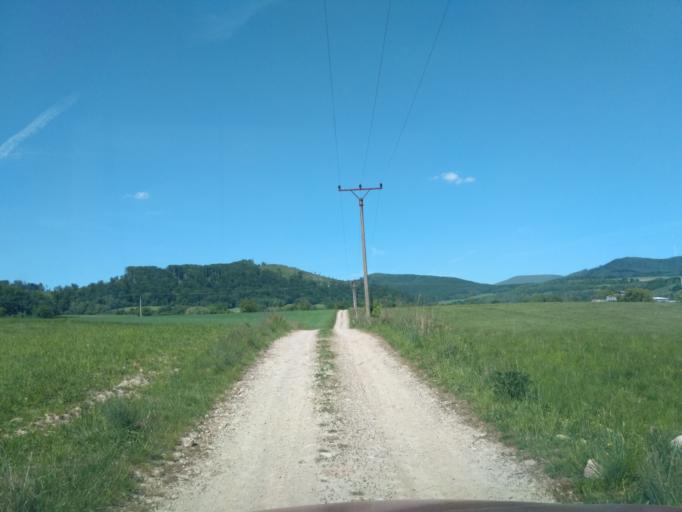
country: SK
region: Presovsky
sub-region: Okres Presov
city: Presov
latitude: 48.8920
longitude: 21.3925
